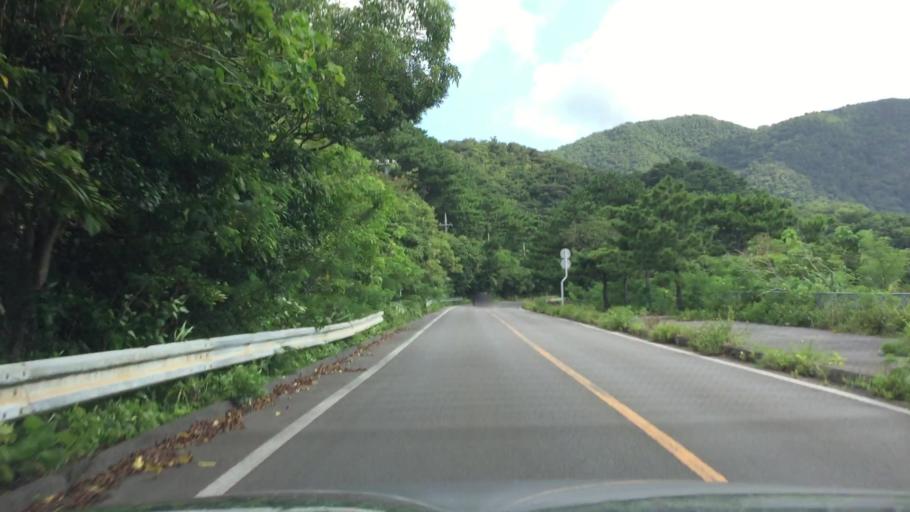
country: JP
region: Okinawa
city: Ishigaki
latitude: 24.4308
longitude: 124.2103
